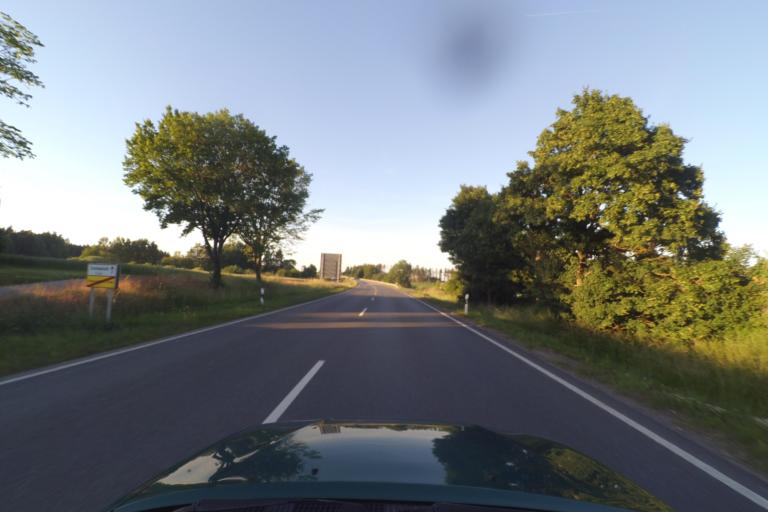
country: DE
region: Bavaria
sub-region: Upper Palatinate
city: Tirschenreuth
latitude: 49.8334
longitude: 12.3087
